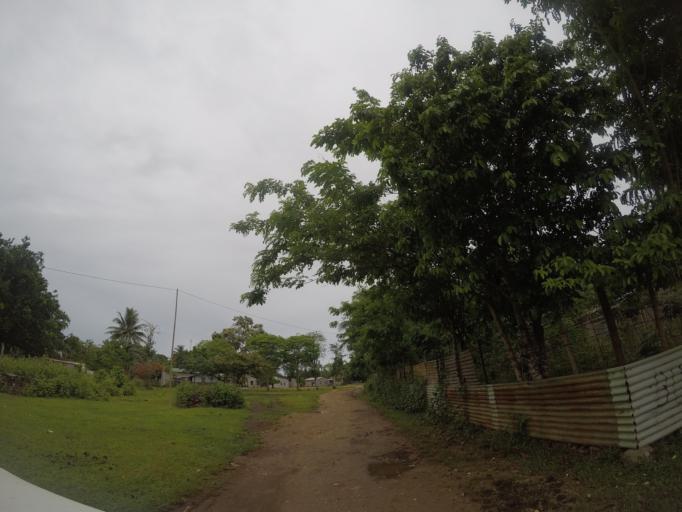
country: TL
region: Lautem
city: Lospalos
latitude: -8.5214
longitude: 127.0069
